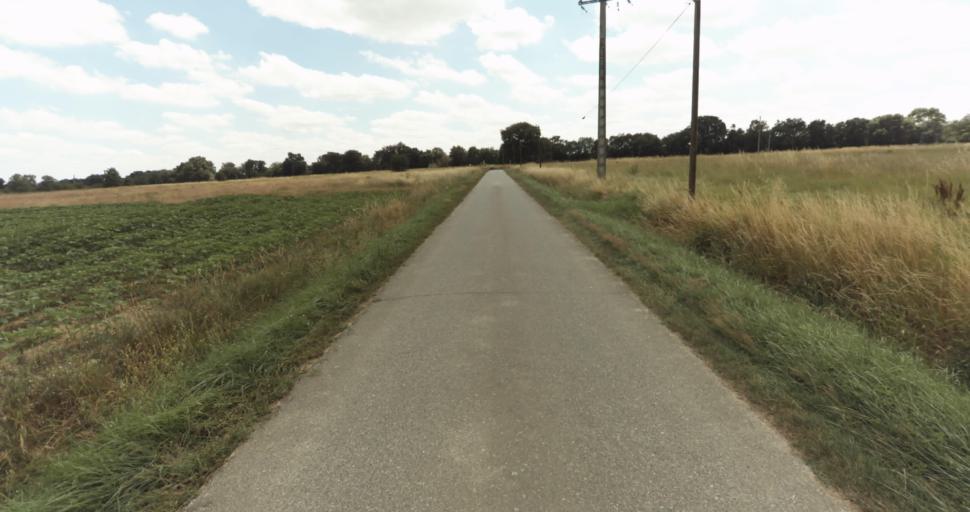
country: FR
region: Midi-Pyrenees
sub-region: Departement de la Haute-Garonne
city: Fontenilles
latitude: 43.5639
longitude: 1.1778
